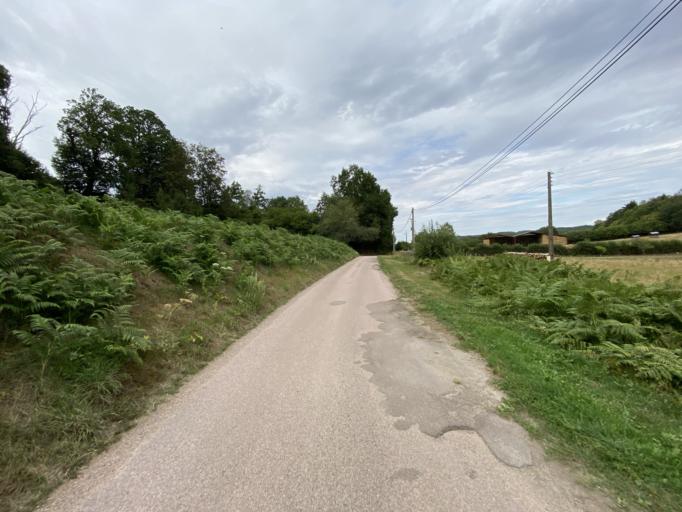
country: FR
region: Bourgogne
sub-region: Departement de la Cote-d'Or
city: Saulieu
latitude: 47.2591
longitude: 4.1353
